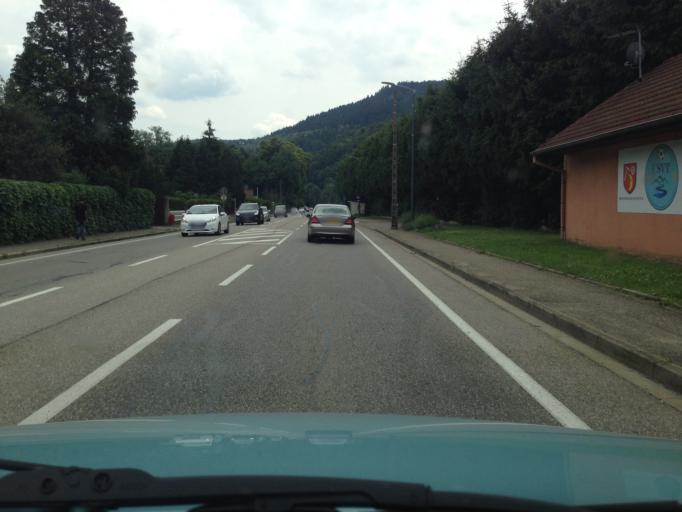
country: FR
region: Alsace
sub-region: Departement du Haut-Rhin
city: Bitschwiller-les-Thann
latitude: 47.8248
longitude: 7.0814
